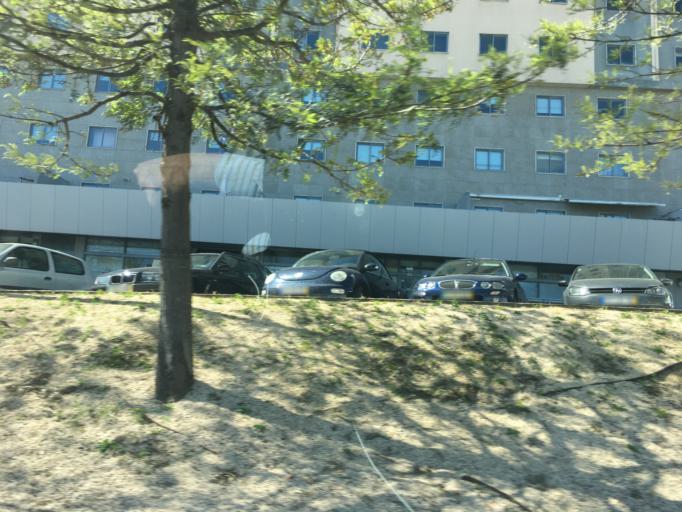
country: PT
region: Lisbon
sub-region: Odivelas
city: Pontinha
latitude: 38.7557
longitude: -9.1671
